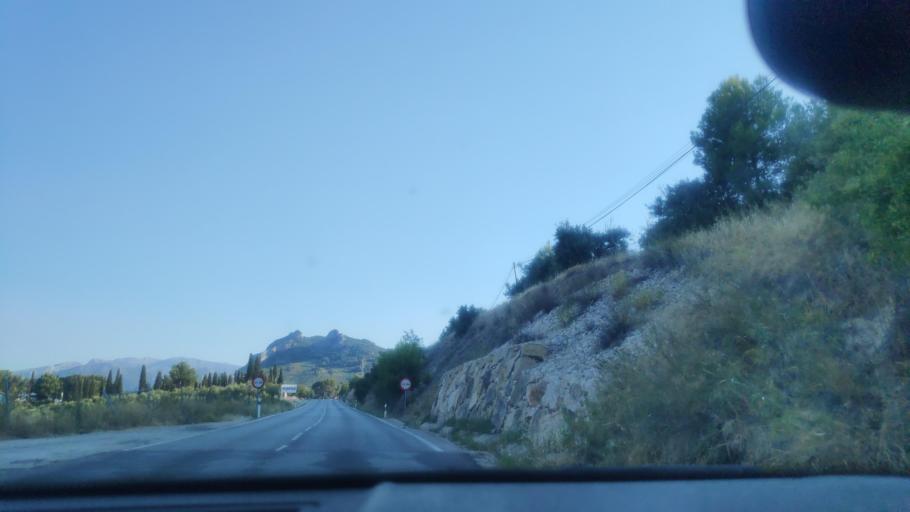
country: ES
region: Andalusia
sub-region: Provincia de Jaen
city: Jaen
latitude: 37.7589
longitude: -3.7901
